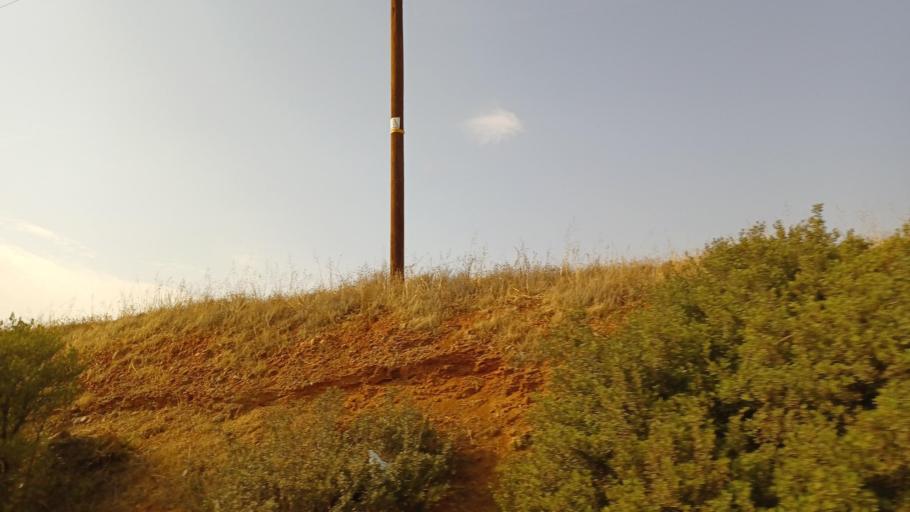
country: CY
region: Lefkosia
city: Astromeritis
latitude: 35.1189
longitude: 33.0082
